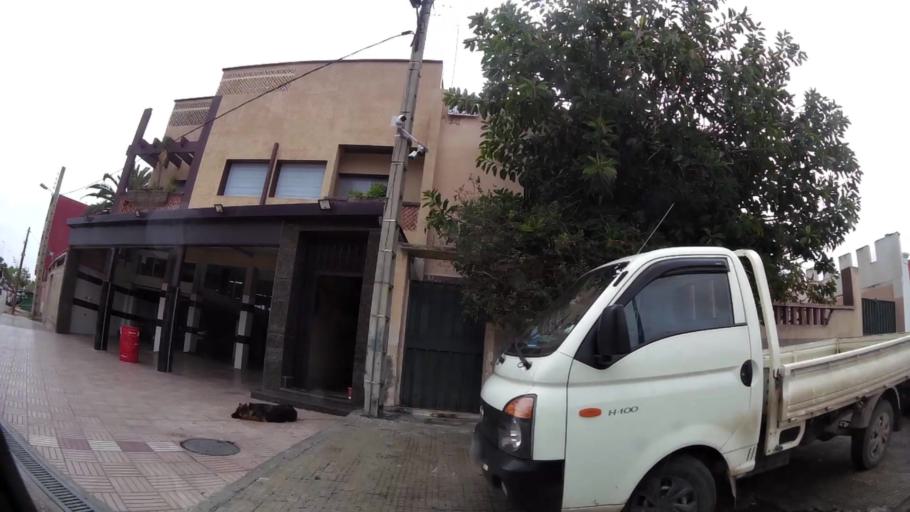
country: MA
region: Grand Casablanca
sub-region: Mediouna
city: Tit Mellil
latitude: 33.6138
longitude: -7.5246
